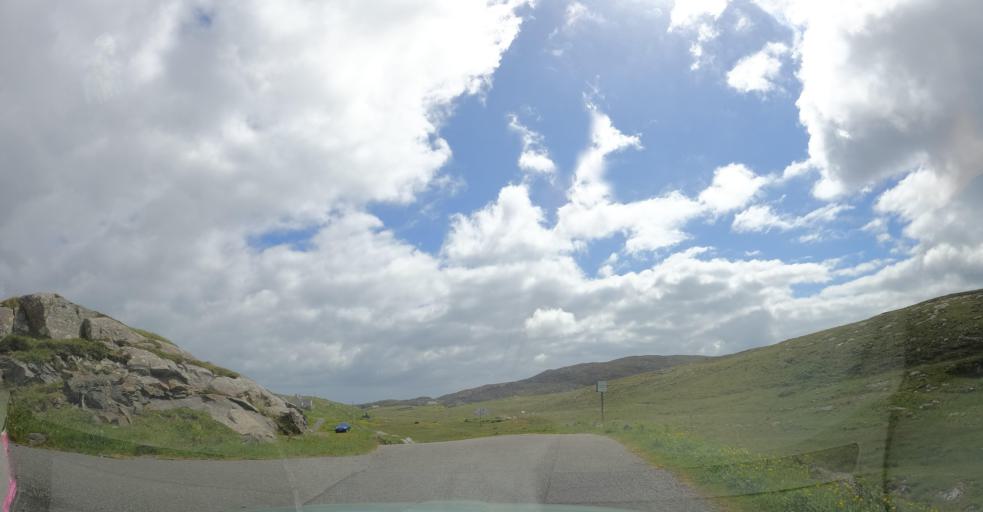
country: GB
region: Scotland
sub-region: Eilean Siar
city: Isle of South Uist
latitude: 57.0723
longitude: -7.2987
